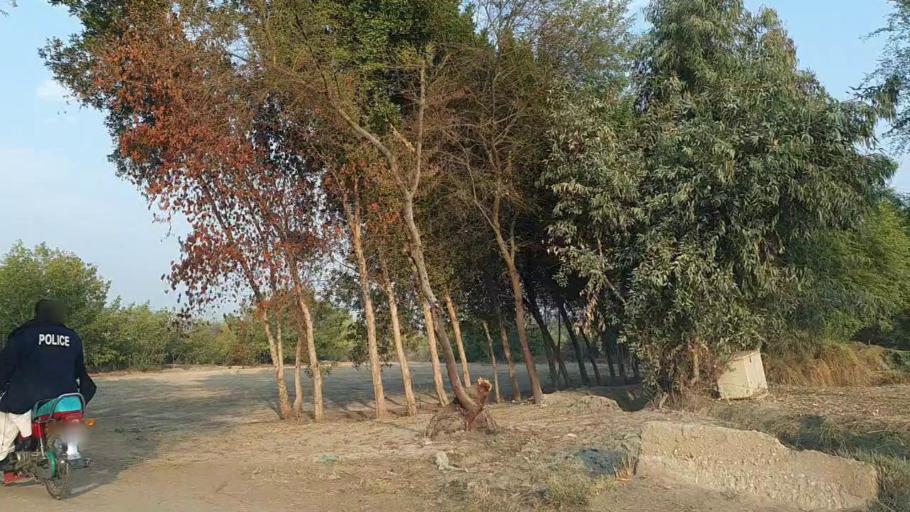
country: PK
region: Sindh
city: Jam Sahib
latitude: 26.3217
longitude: 68.5510
